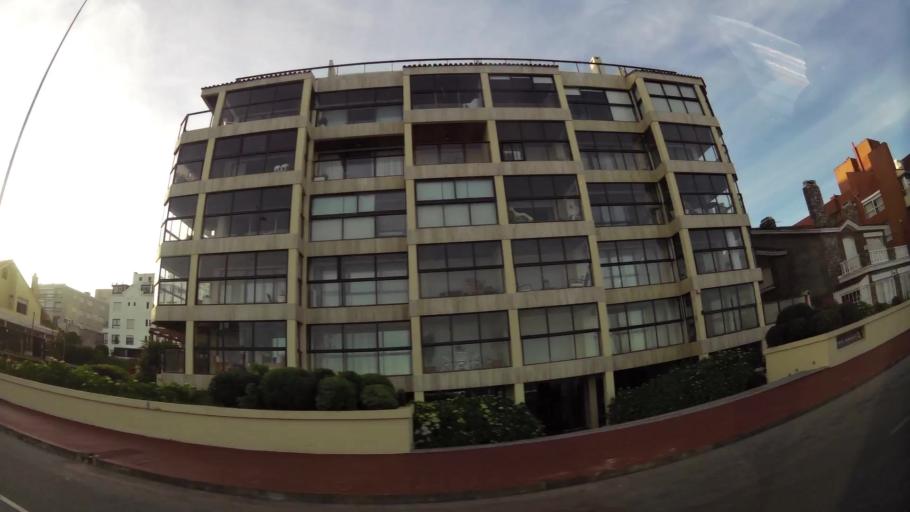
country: UY
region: Maldonado
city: Punta del Este
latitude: -34.9628
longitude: -54.9409
